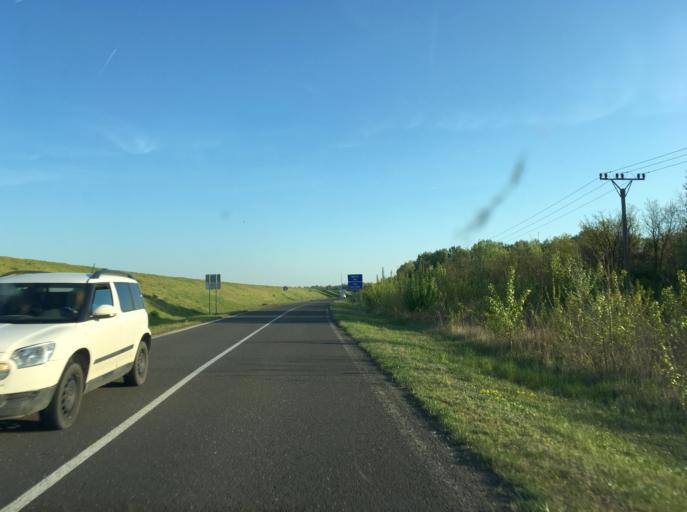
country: HU
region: Gyor-Moson-Sopron
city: Rajka
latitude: 48.0156
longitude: 17.2518
